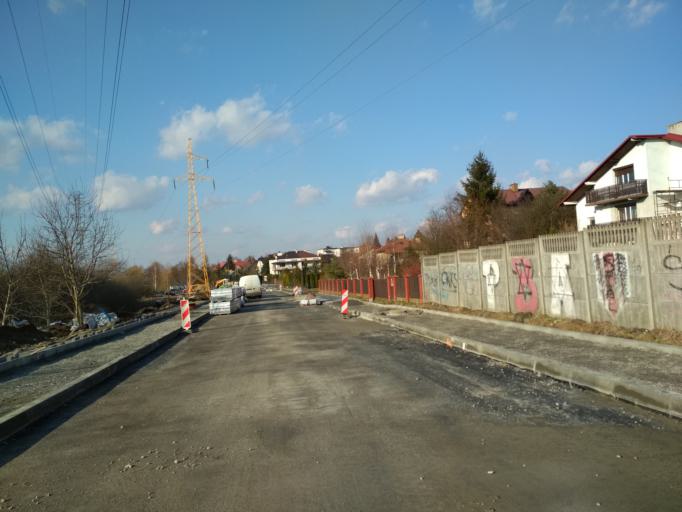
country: PL
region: Subcarpathian Voivodeship
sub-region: Rzeszow
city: Rzeszow
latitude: 50.0476
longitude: 21.9640
